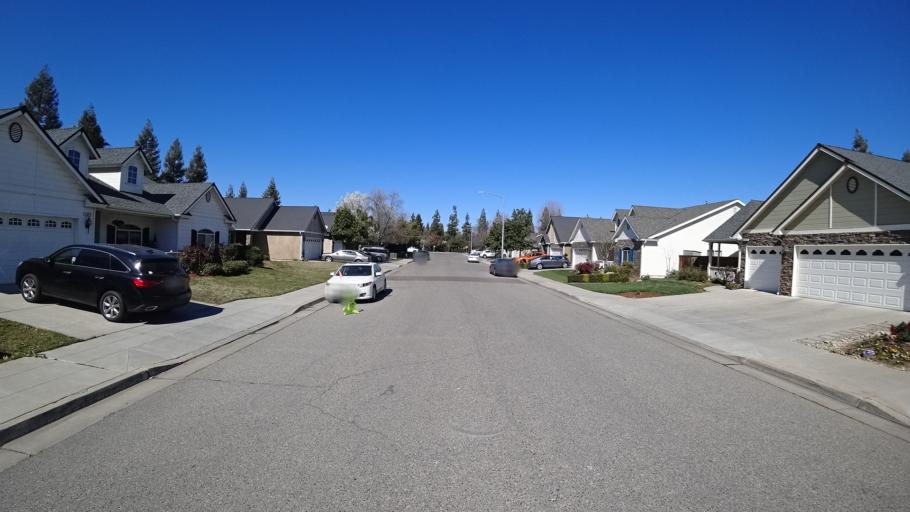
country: US
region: California
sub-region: Fresno County
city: Clovis
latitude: 36.8507
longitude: -119.7451
